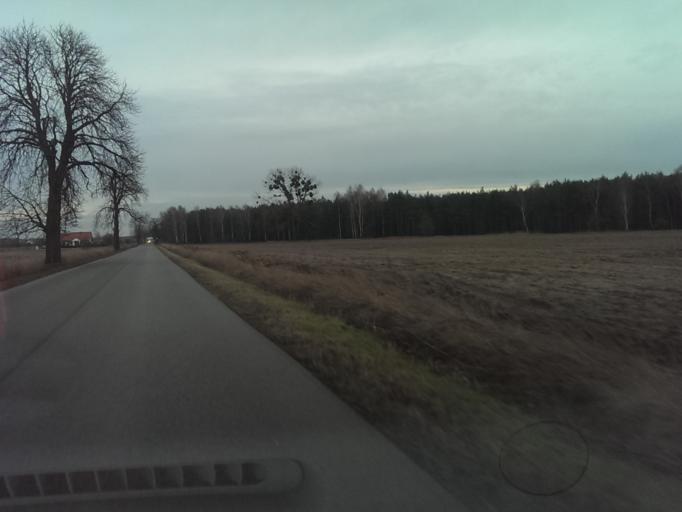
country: PL
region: Kujawsko-Pomorskie
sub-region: Powiat nakielski
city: Szubin
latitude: 53.0810
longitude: 17.7823
